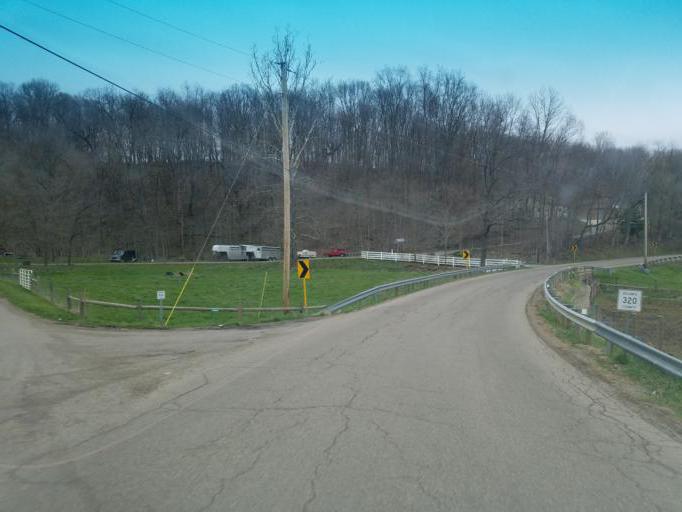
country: US
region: Ohio
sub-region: Holmes County
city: Millersburg
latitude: 40.6002
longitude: -81.9717
